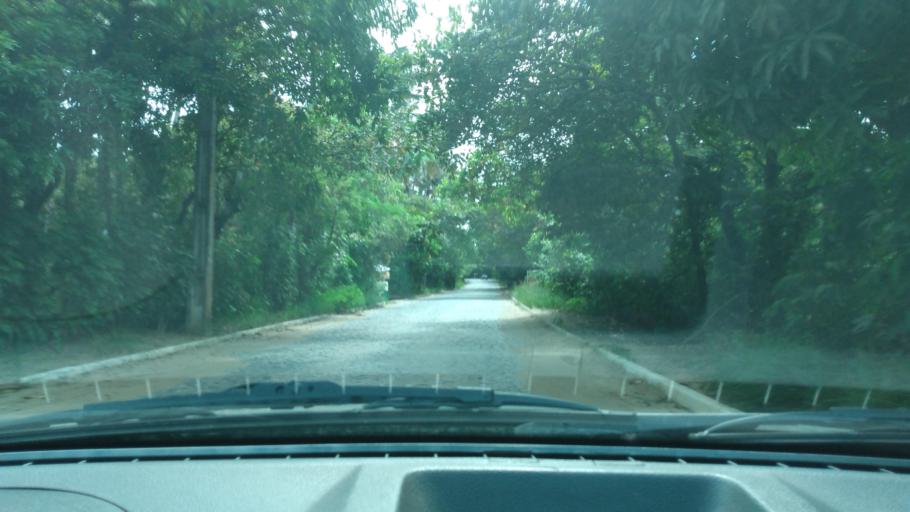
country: BR
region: Pernambuco
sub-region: Cabo De Santo Agostinho
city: Cabo
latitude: -8.3474
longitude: -34.9538
